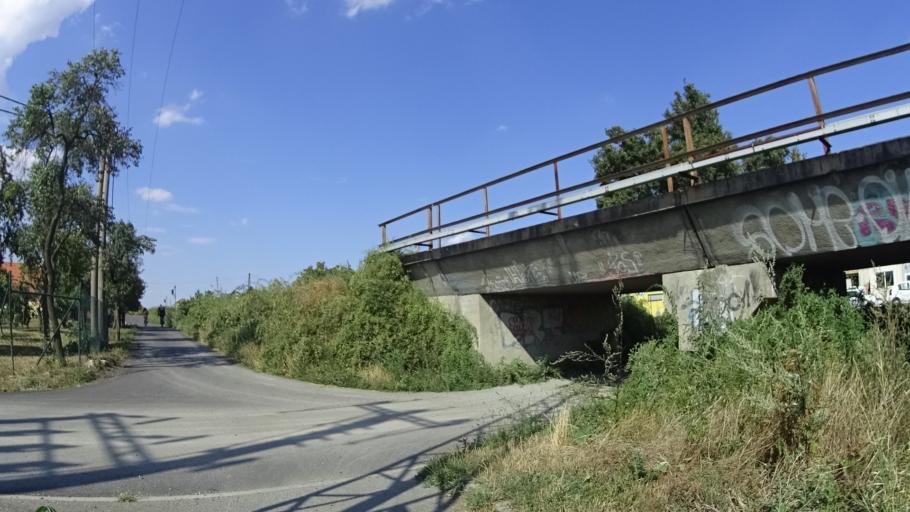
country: CZ
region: Zlin
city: Kunovice
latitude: 49.0456
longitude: 17.4621
